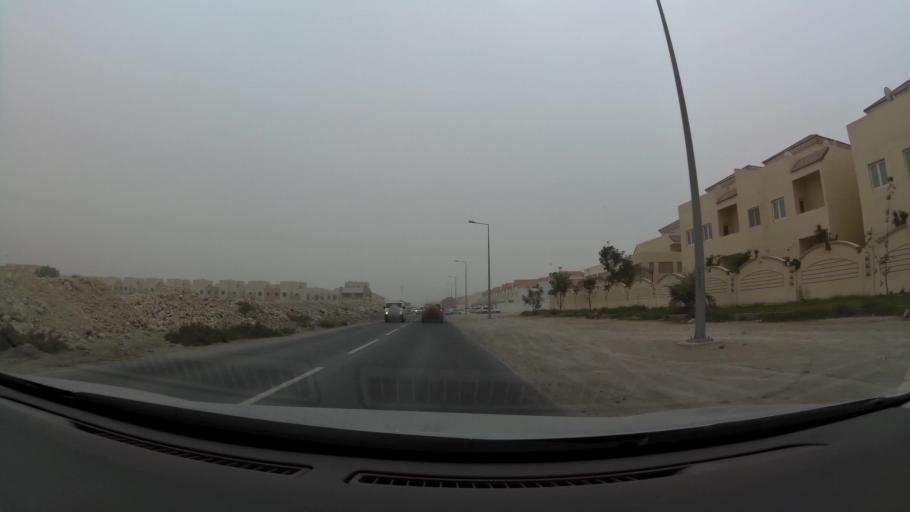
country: QA
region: Baladiyat ad Dawhah
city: Doha
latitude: 25.2435
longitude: 51.4910
